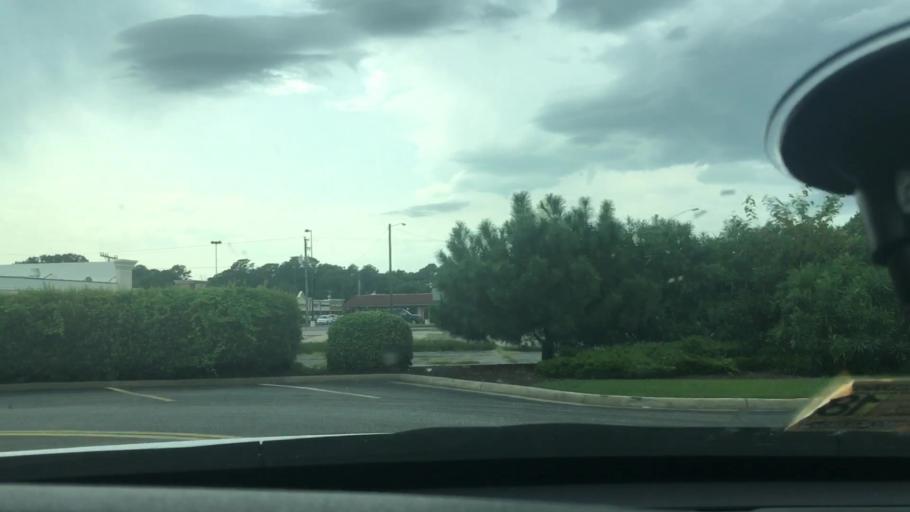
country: US
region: Virginia
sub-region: City of Norfolk
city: Norfolk
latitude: 36.9039
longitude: -76.1346
